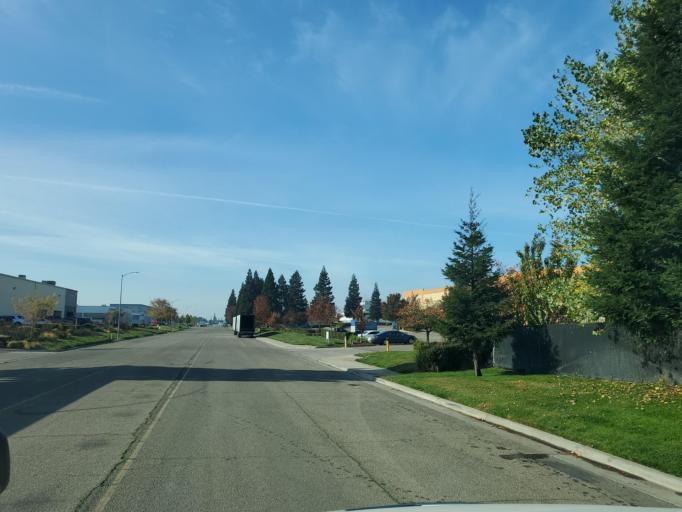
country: US
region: California
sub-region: San Joaquin County
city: Kennedy
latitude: 37.9094
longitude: -121.2146
